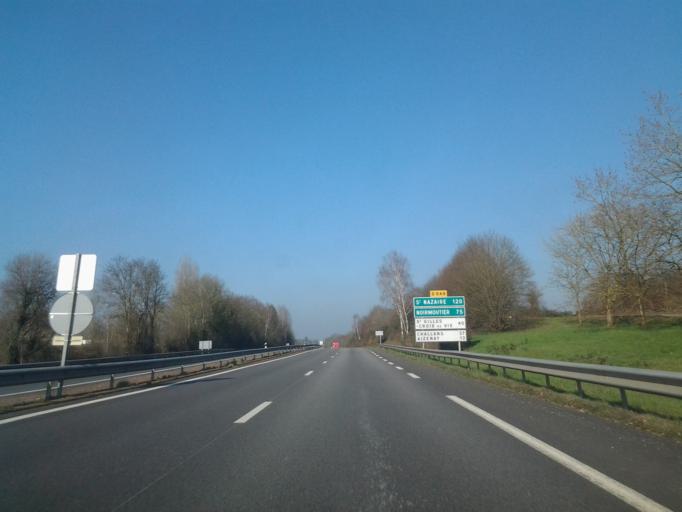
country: FR
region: Pays de la Loire
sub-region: Departement de la Vendee
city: La Roche-sur-Yon
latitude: 46.6857
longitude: -1.4533
